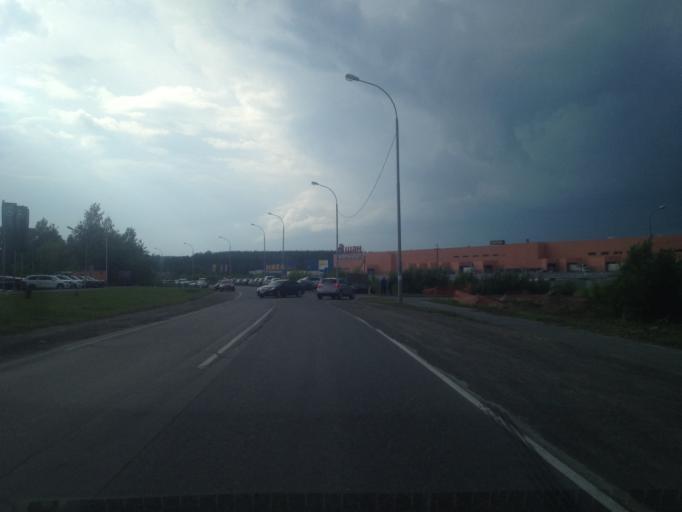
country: RU
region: Sverdlovsk
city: Shirokaya Rechka
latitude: 56.8203
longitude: 60.5083
